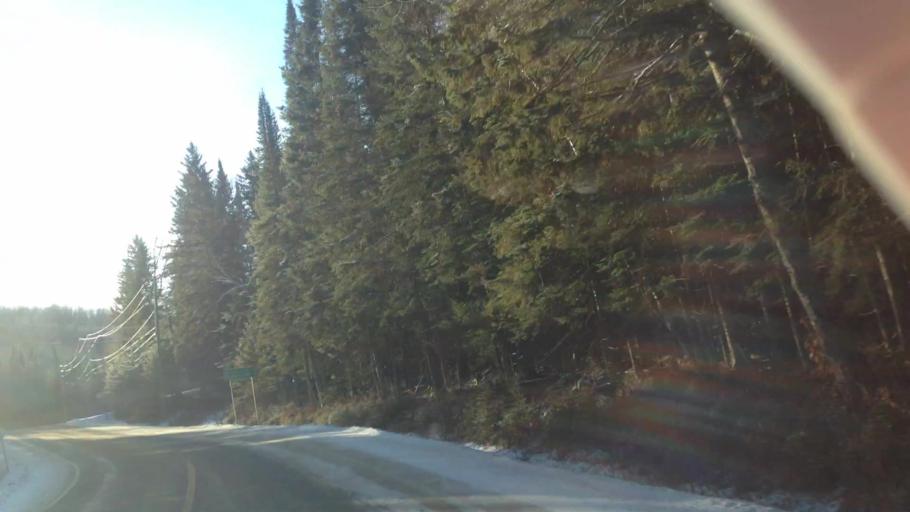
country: CA
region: Quebec
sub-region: Laurentides
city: Mont-Tremblant
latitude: 45.9364
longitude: -74.5437
